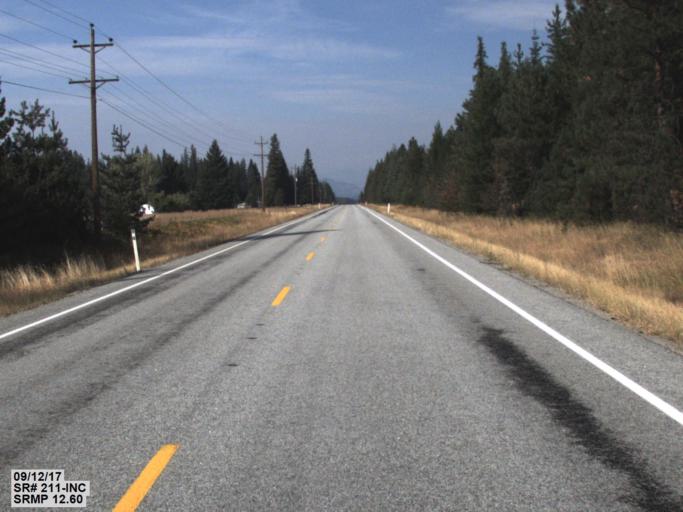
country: US
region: Washington
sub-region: Pend Oreille County
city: Newport
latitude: 48.2678
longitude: -117.2845
